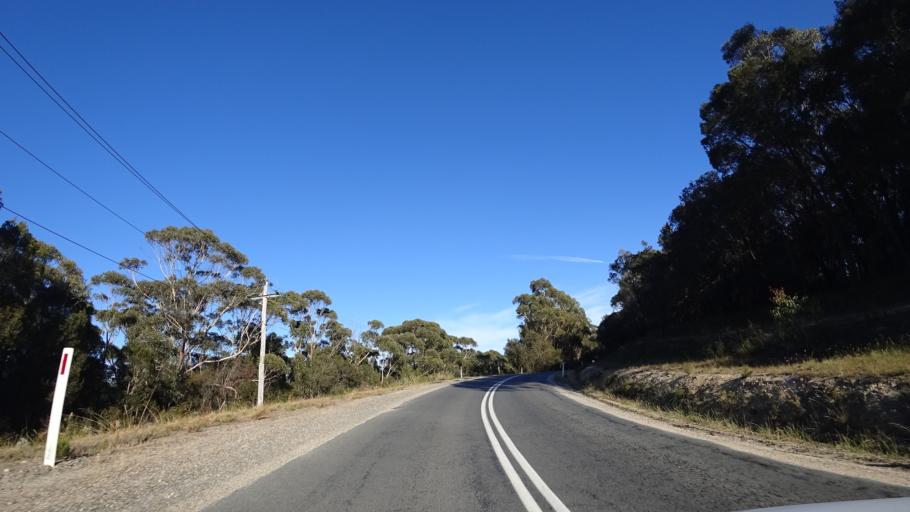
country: AU
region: Tasmania
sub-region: Break O'Day
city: St Helens
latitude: -41.3078
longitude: 148.2196
